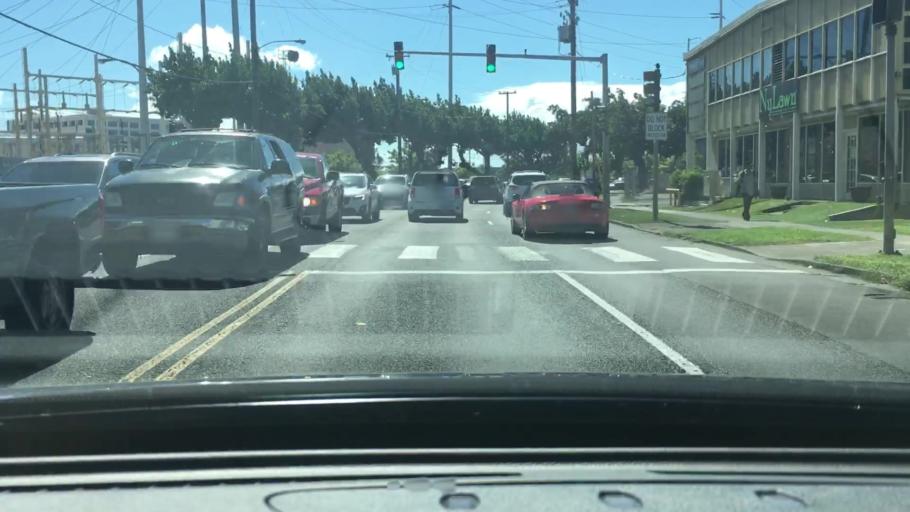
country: US
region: Hawaii
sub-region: Honolulu County
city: Honolulu
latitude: 21.3184
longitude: -157.8660
